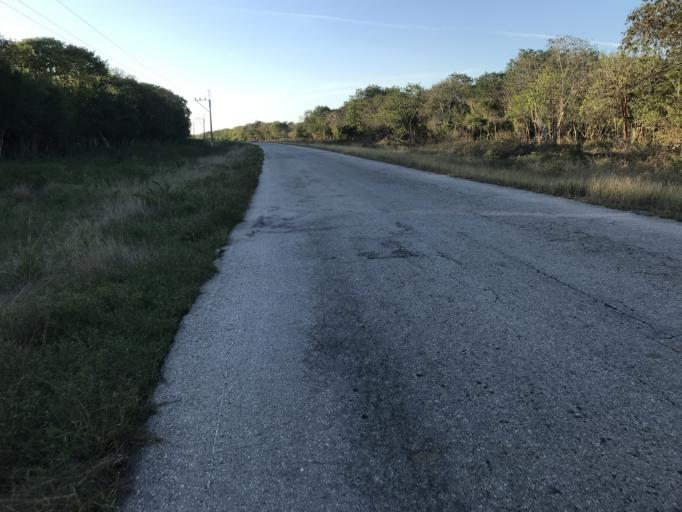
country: CU
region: Cienfuegos
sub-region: Municipio de Aguada de Pasajeros
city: Aguada de Pasajeros
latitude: 22.0753
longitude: -81.0605
